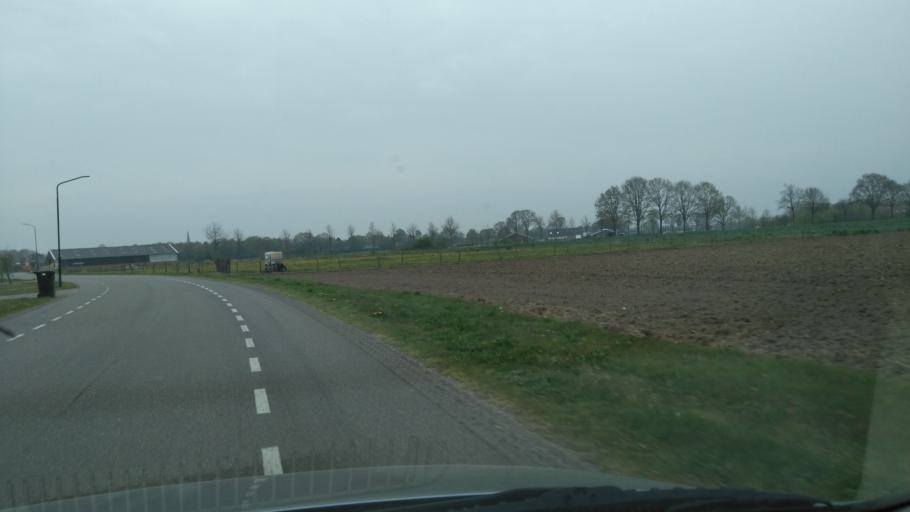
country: NL
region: North Brabant
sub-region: Gemeente Baarle-Nassau
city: Baarle-Nassau
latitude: 51.4759
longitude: 4.9677
